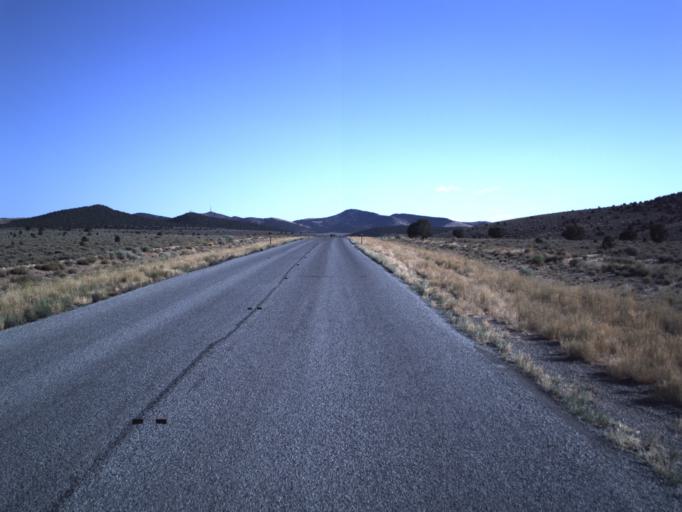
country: US
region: Utah
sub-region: Iron County
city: Parowan
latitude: 38.0233
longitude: -112.9981
